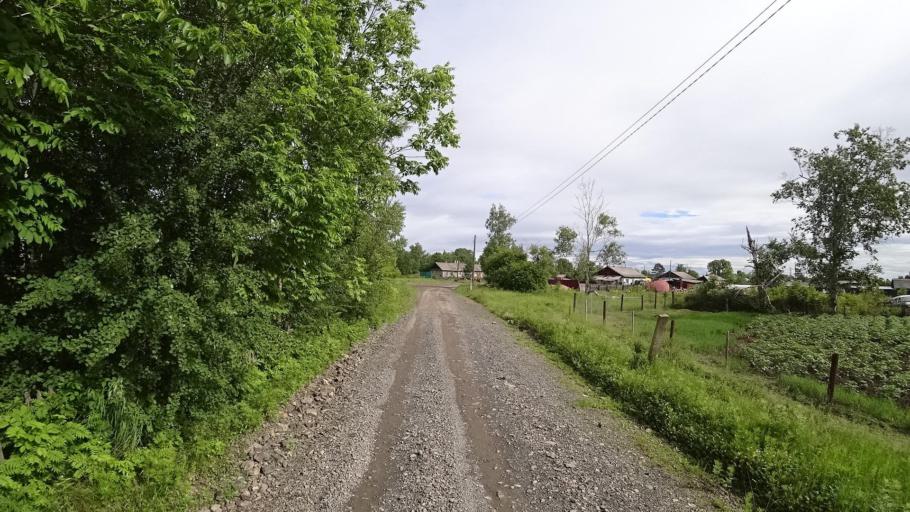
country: RU
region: Khabarovsk Krai
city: Amursk
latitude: 49.8910
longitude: 136.1298
